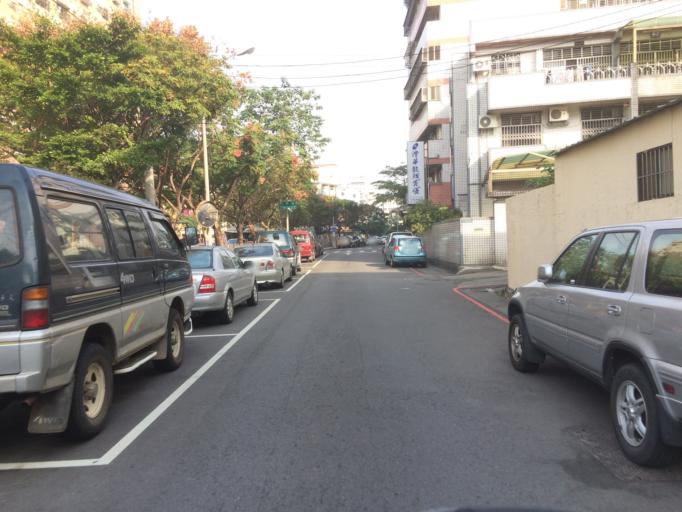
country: TW
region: Taiwan
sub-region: Taichung City
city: Taichung
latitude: 24.1750
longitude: 120.6934
